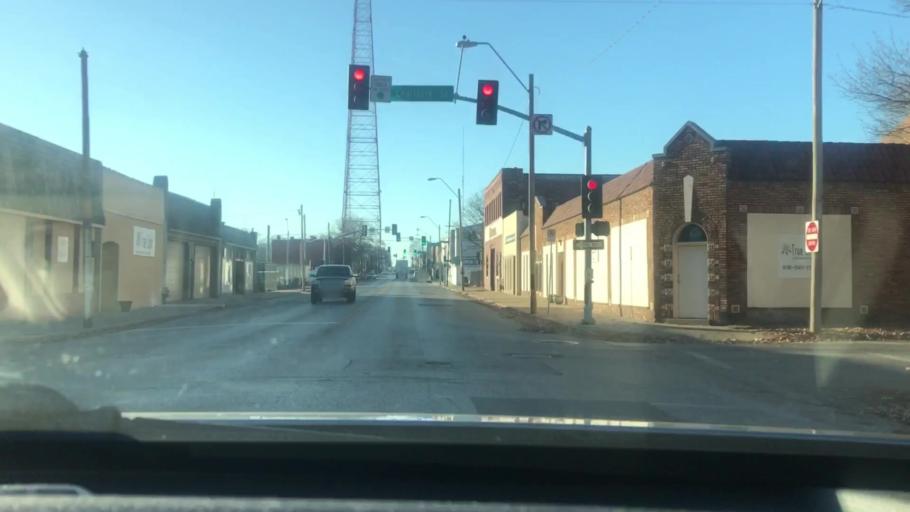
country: US
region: Missouri
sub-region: Jackson County
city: Kansas City
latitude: 39.0707
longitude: -94.5753
